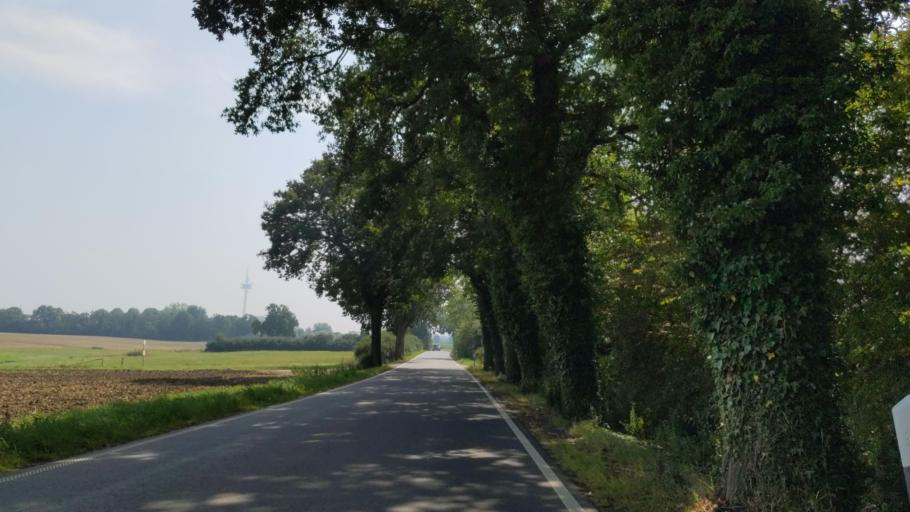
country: DE
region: Schleswig-Holstein
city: Stockelsdorf
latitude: 53.9168
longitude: 10.6239
